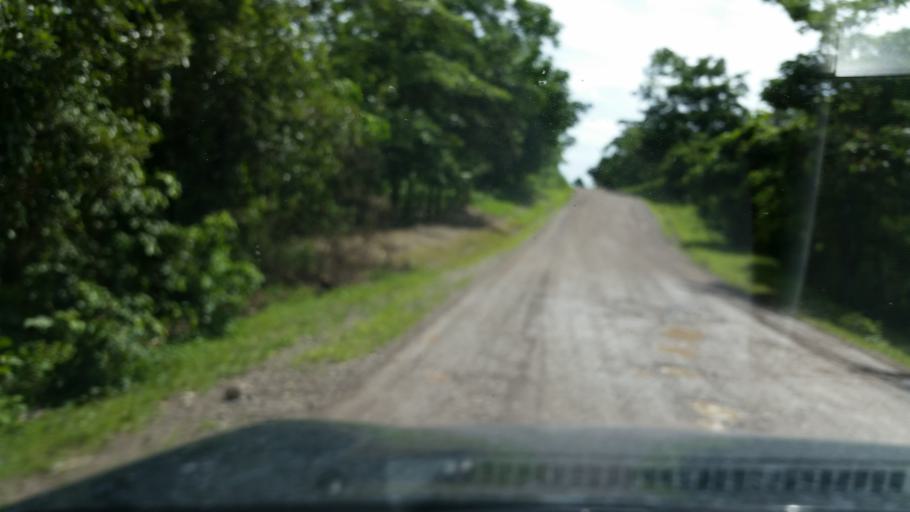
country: NI
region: Atlantico Norte (RAAN)
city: Siuna
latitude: 13.6816
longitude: -84.6447
